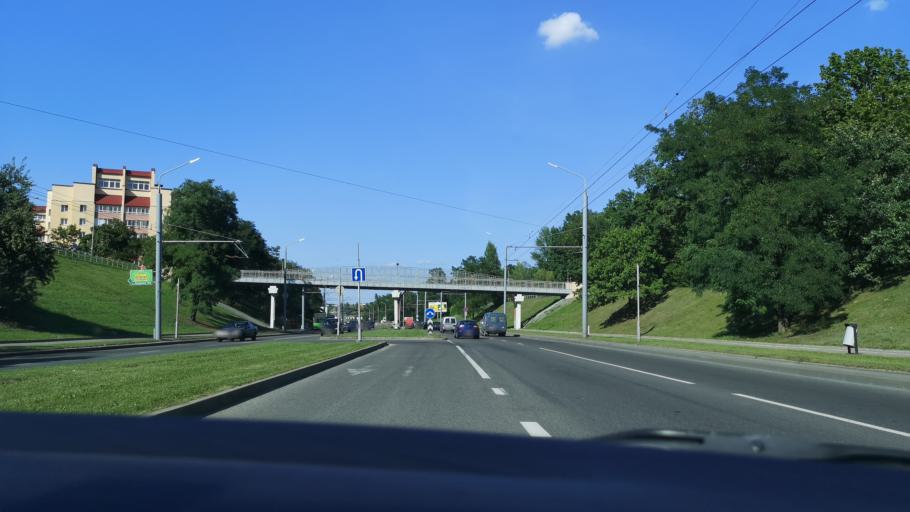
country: BY
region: Grodnenskaya
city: Hrodna
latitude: 53.6553
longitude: 23.8570
